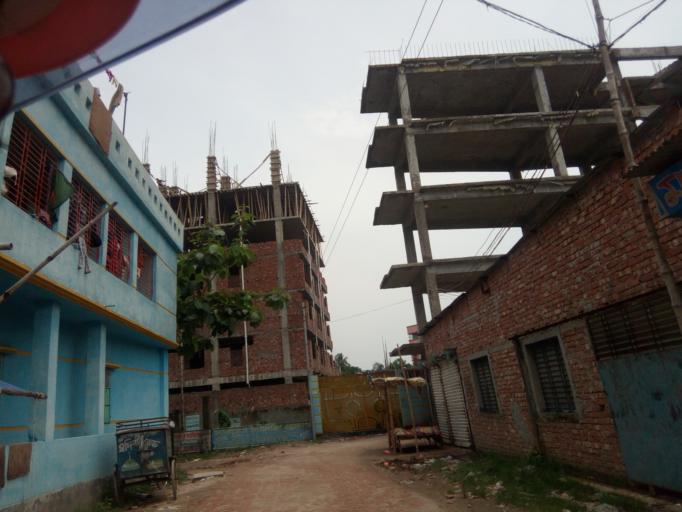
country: BD
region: Dhaka
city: Azimpur
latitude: 23.7436
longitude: 90.3486
